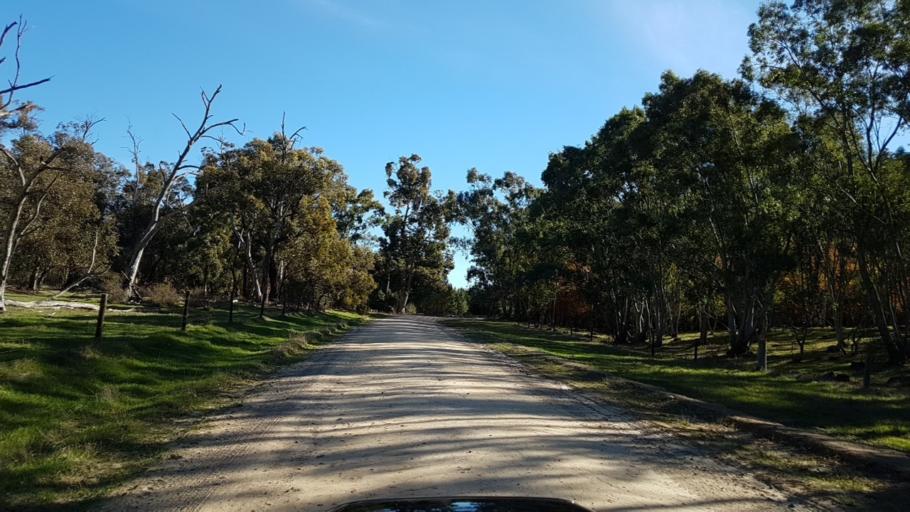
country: AU
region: South Australia
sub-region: Northern Areas
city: Jamestown
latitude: -33.2858
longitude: 138.5634
